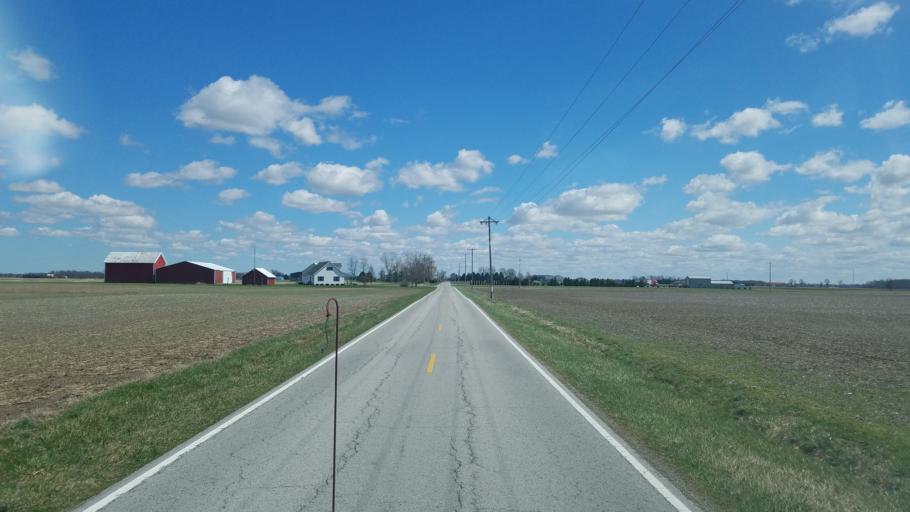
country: US
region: Ohio
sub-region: Hancock County
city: Findlay
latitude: 41.0069
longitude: -83.5386
